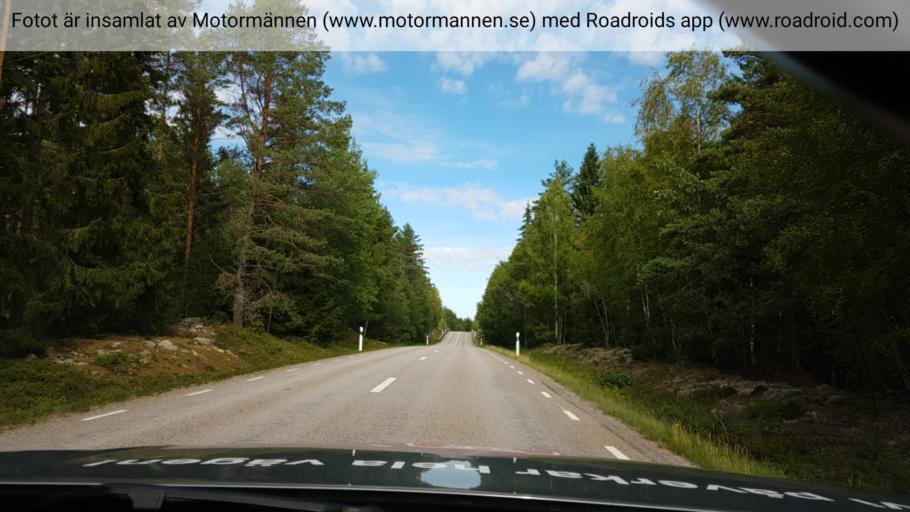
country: SE
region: Uppsala
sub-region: Heby Kommun
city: OEstervala
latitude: 60.0035
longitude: 17.3020
